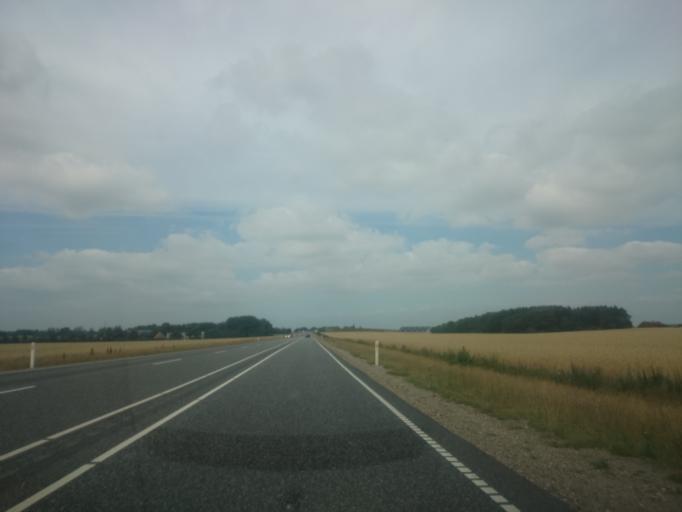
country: DK
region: South Denmark
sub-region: Vejle Kommune
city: Egtved
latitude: 55.7101
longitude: 9.2299
